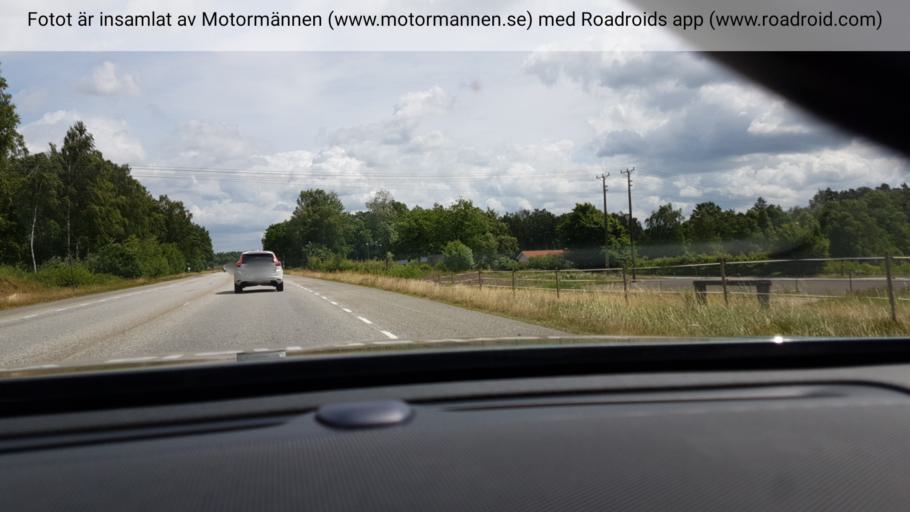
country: SE
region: Skane
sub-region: Hassleholms Kommun
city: Hassleholm
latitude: 56.1696
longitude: 13.8059
